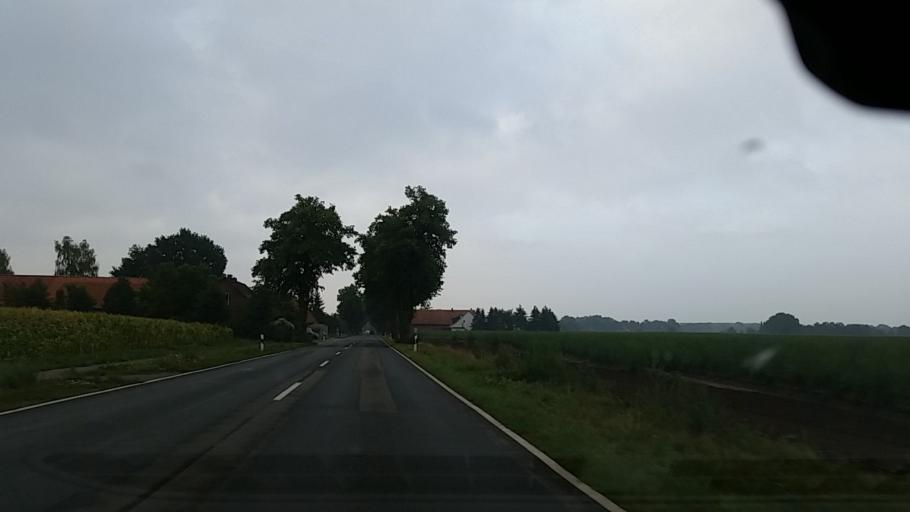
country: DE
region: Lower Saxony
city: Bodenteich
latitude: 52.8057
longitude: 10.7042
